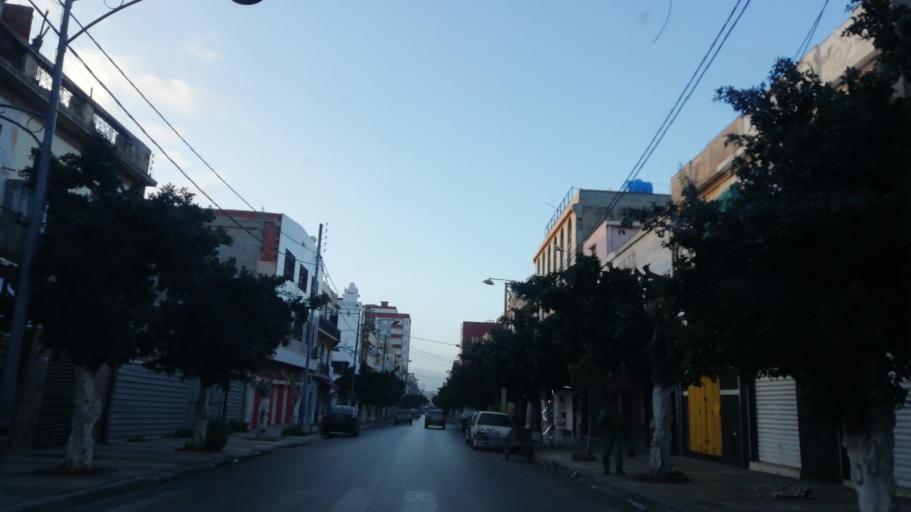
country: DZ
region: Oran
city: Oran
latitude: 35.6843
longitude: -0.6552
